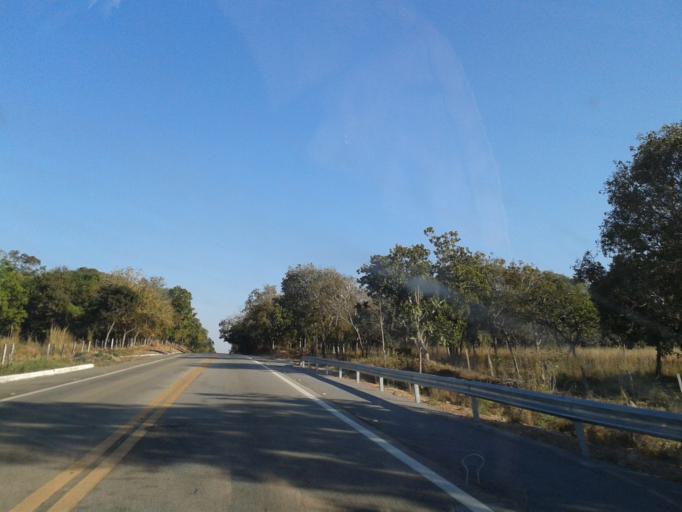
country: BR
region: Goias
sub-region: Itapuranga
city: Itapuranga
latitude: -15.3297
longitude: -50.4220
